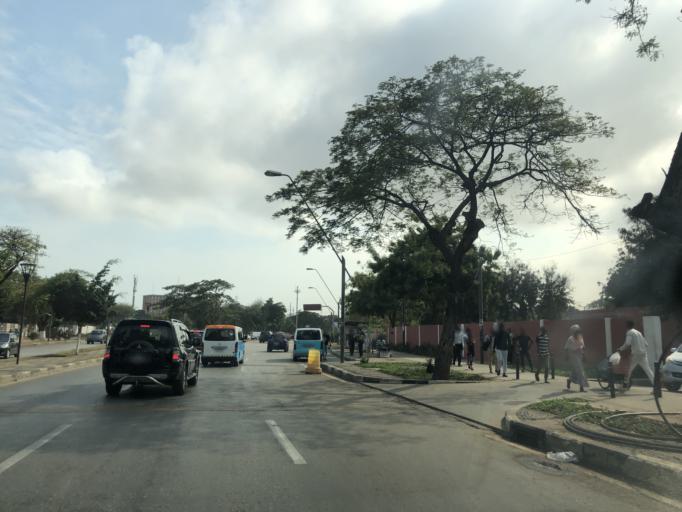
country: AO
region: Luanda
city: Luanda
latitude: -8.8343
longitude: 13.2388
